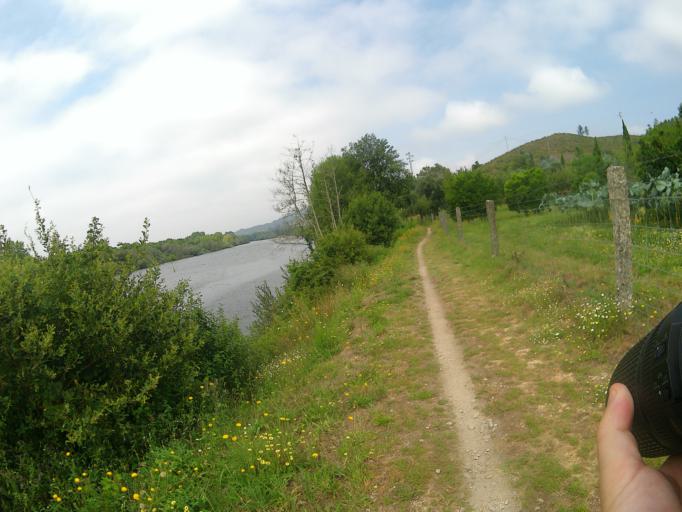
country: PT
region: Viana do Castelo
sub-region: Ponte de Lima
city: Ponte de Lima
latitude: 41.7783
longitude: -8.5692
